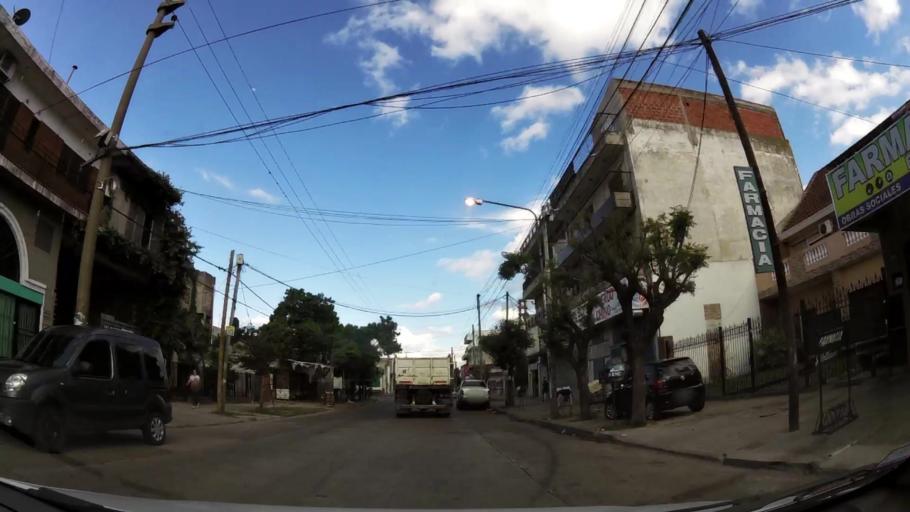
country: AR
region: Buenos Aires
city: San Justo
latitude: -34.6999
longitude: -58.5918
